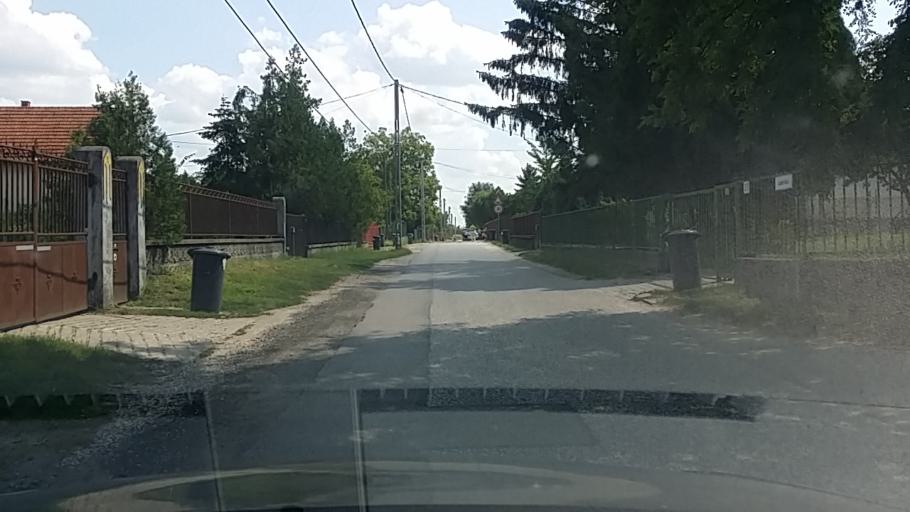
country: HU
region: Pest
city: Halasztelek
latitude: 47.3803
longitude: 19.0128
